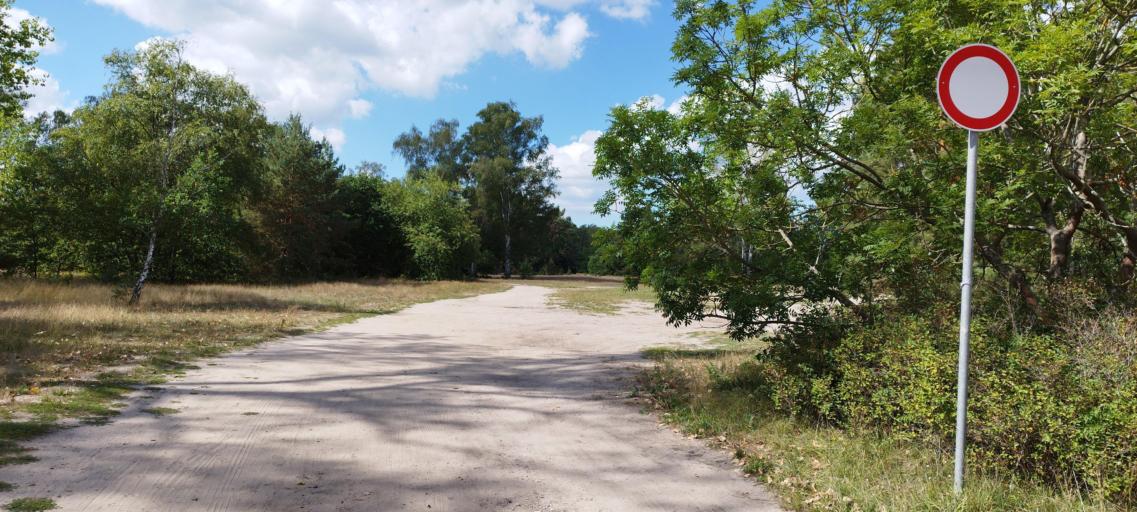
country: DE
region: Brandenburg
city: Rathenow
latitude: 52.5941
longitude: 12.3719
